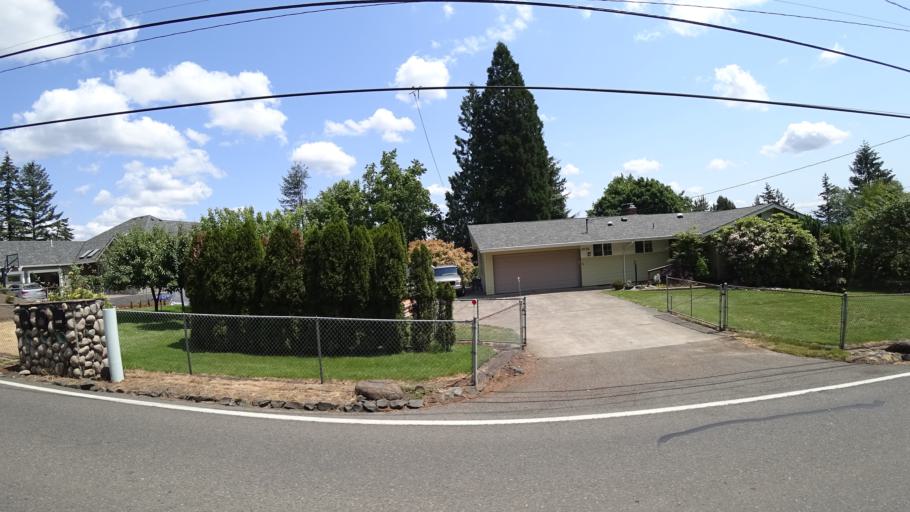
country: US
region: Oregon
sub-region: Clackamas County
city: Happy Valley
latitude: 45.4499
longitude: -122.5431
